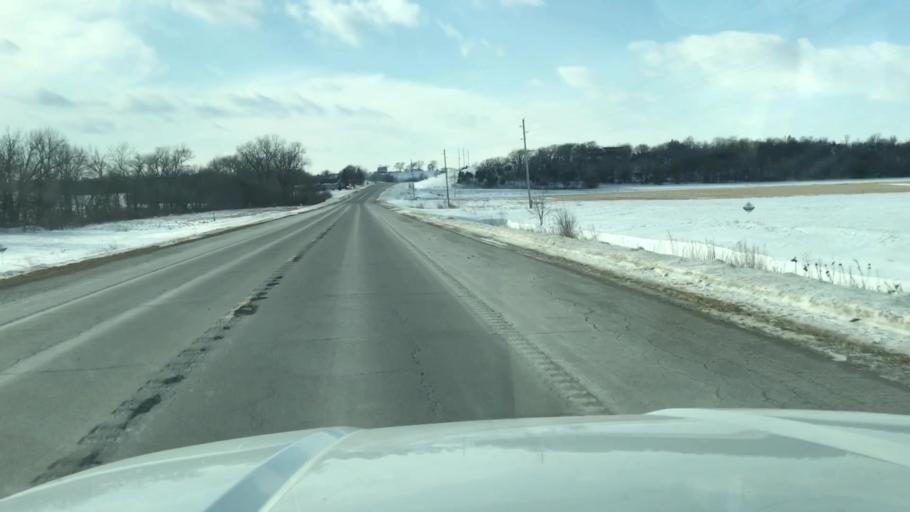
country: US
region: Missouri
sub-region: Nodaway County
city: Maryville
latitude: 40.3442
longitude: -94.6885
